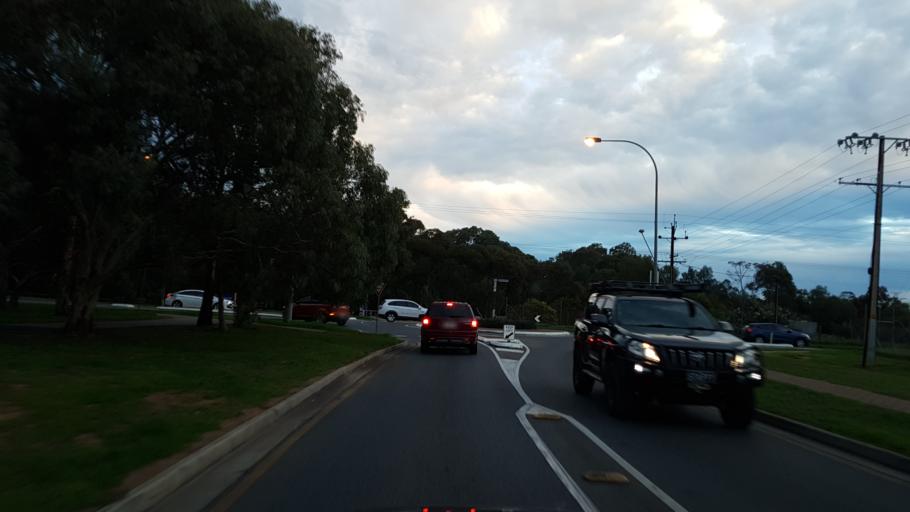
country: AU
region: South Australia
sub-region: Salisbury
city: Salisbury
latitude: -34.7614
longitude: 138.6196
